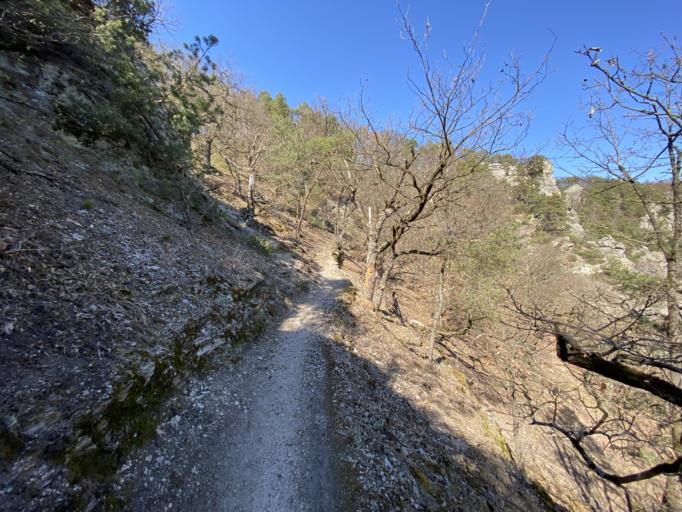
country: AT
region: Lower Austria
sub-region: Politischer Bezirk Krems
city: Durnstein
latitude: 48.4078
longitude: 15.5244
